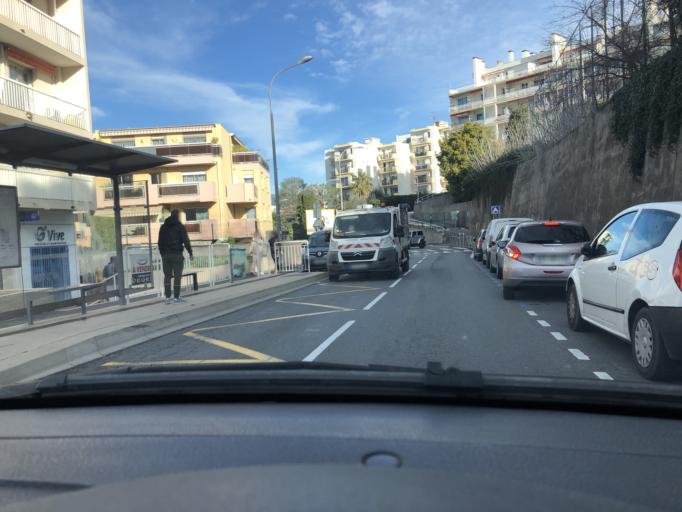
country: FR
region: Provence-Alpes-Cote d'Azur
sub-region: Departement des Alpes-Maritimes
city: Saint-Laurent-du-Var
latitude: 43.6786
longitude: 7.2107
